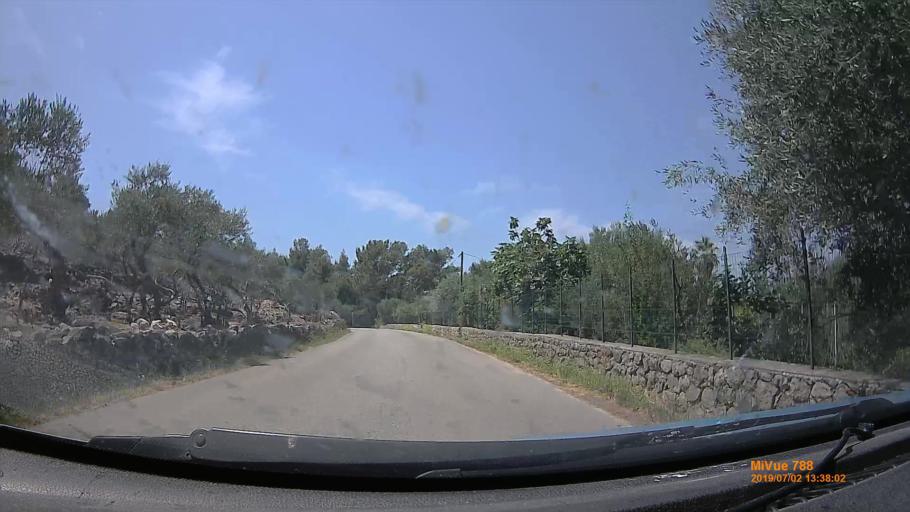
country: HR
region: Primorsko-Goranska
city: Mali Losinj
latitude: 44.5267
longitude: 14.4878
